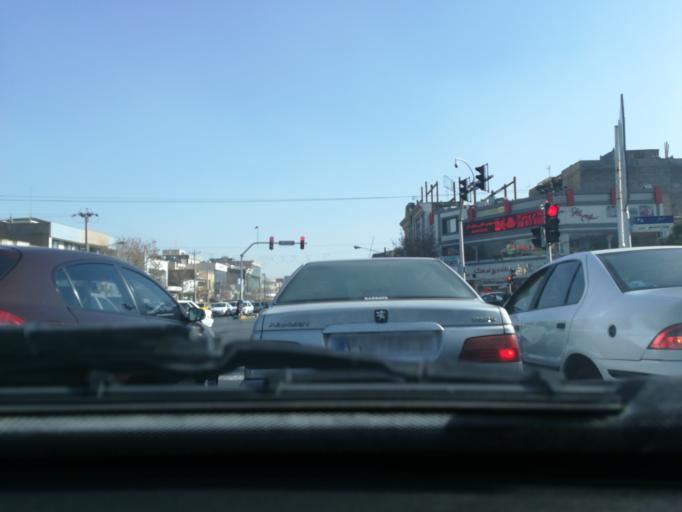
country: IR
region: Razavi Khorasan
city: Mashhad
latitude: 36.3355
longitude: 59.5050
